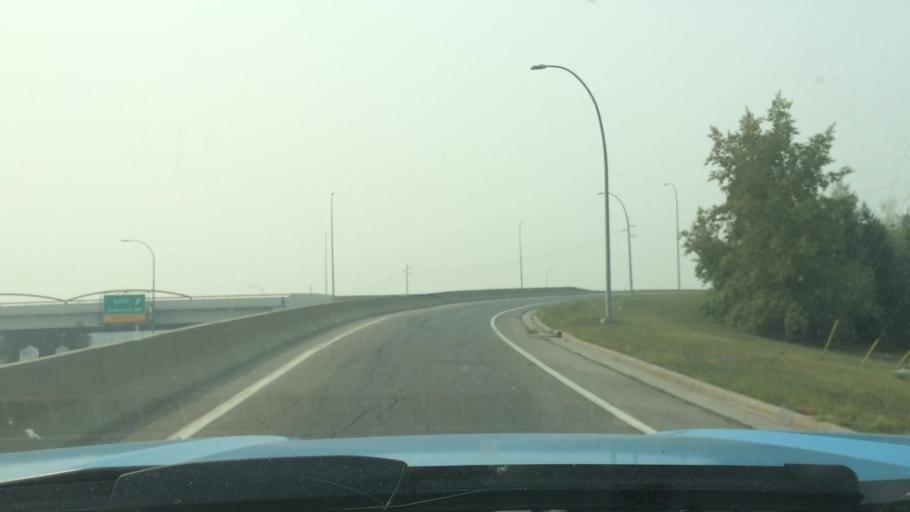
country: CA
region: Alberta
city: Calgary
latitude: 50.9516
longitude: -114.0718
